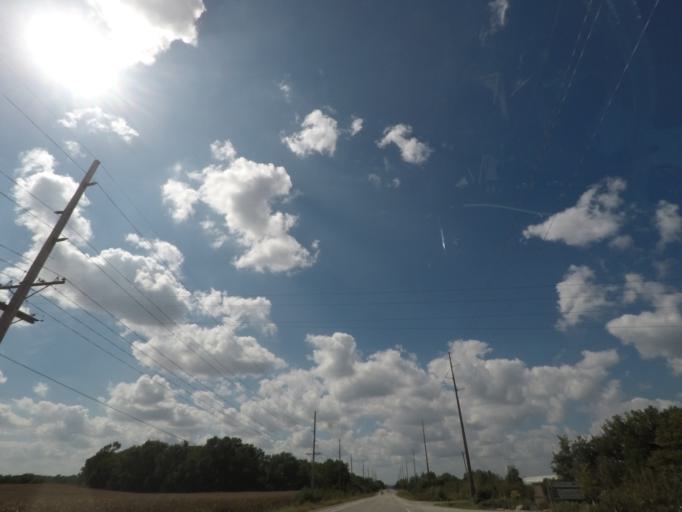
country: US
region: Iowa
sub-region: Story County
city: Ames
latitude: 42.0230
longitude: -93.5607
